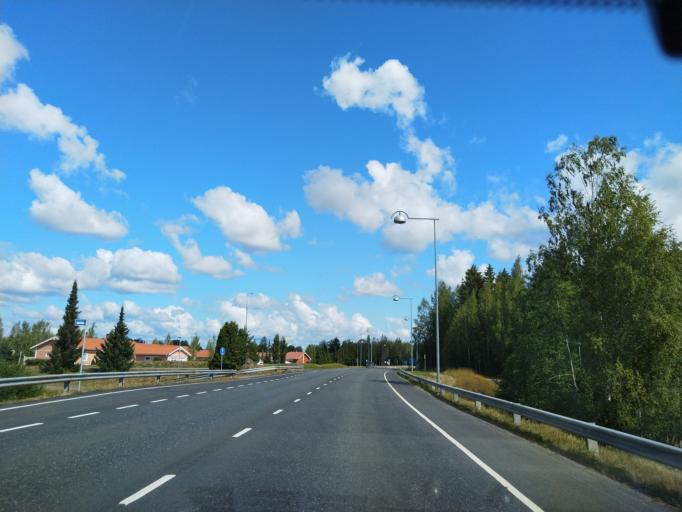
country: FI
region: Satakunta
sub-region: Pori
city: Huittinen
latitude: 61.1713
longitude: 22.7084
